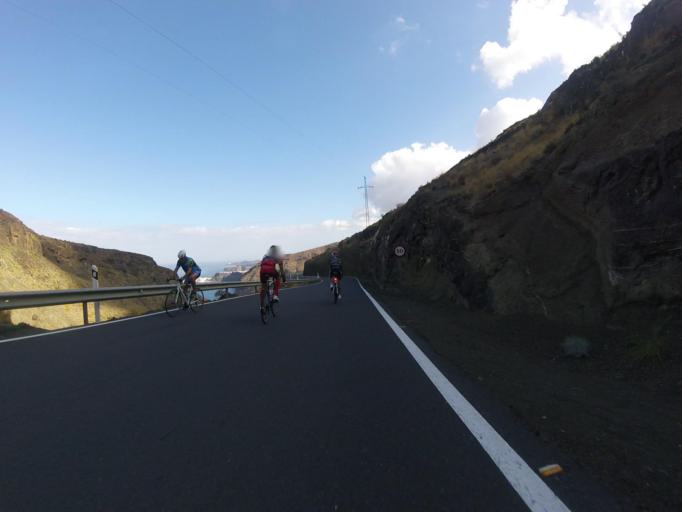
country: ES
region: Canary Islands
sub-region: Provincia de Las Palmas
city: Agaete
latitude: 28.0773
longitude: -15.7082
